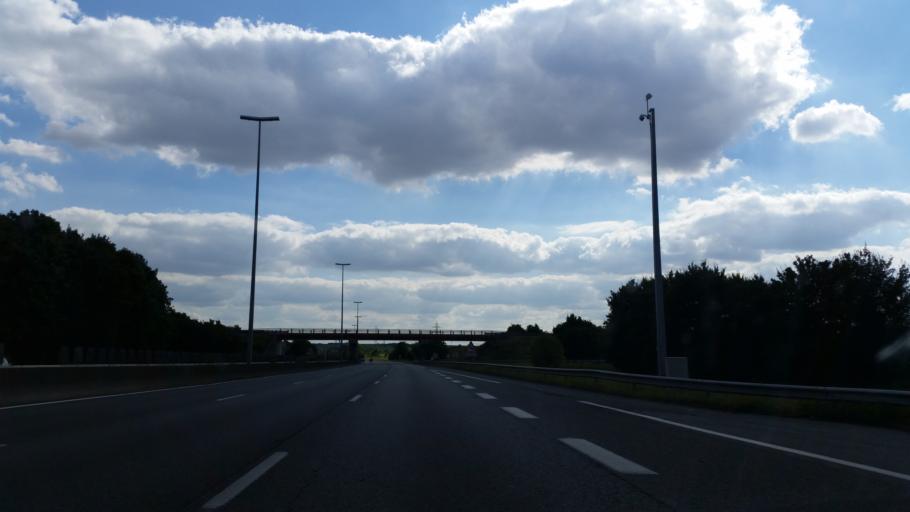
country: FR
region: Nord-Pas-de-Calais
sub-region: Departement du Pas-de-Calais
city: Roeux
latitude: 50.3114
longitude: 2.8961
